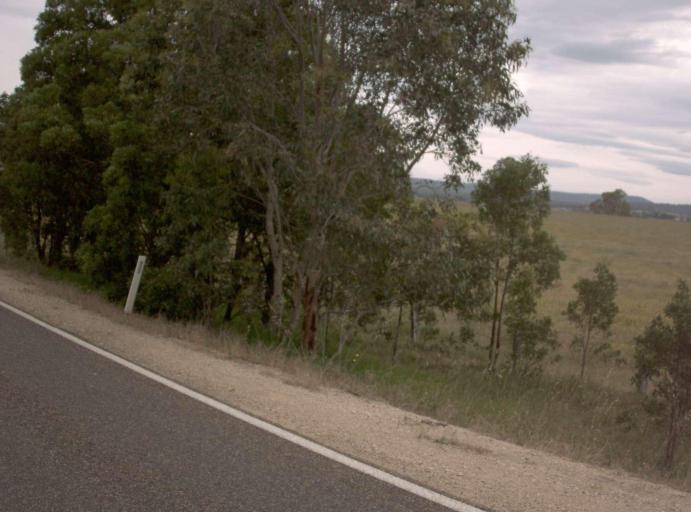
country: AU
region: Victoria
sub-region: East Gippsland
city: Bairnsdale
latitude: -37.8220
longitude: 147.5038
